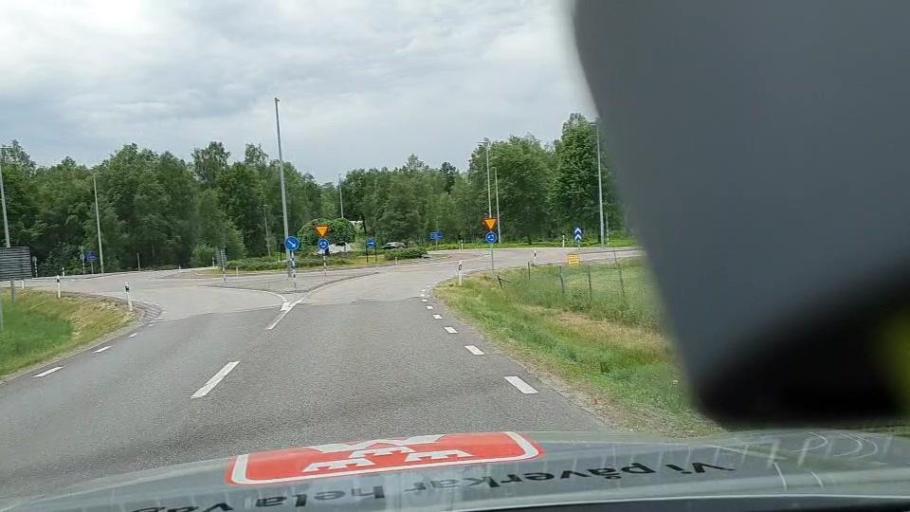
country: SE
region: Kronoberg
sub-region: Lessebo Kommun
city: Lessebo
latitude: 56.5525
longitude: 15.2681
